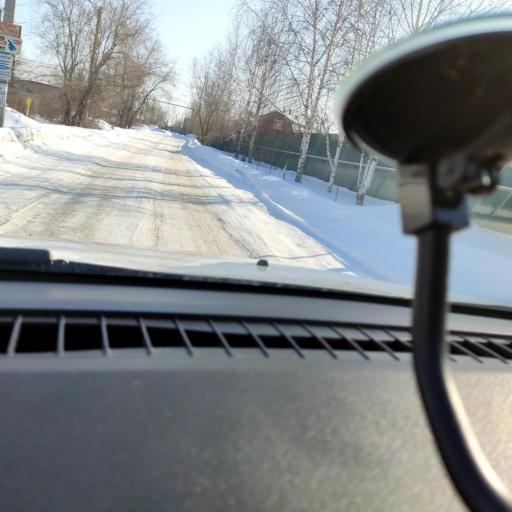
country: RU
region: Samara
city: Samara
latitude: 53.1380
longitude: 50.2443
